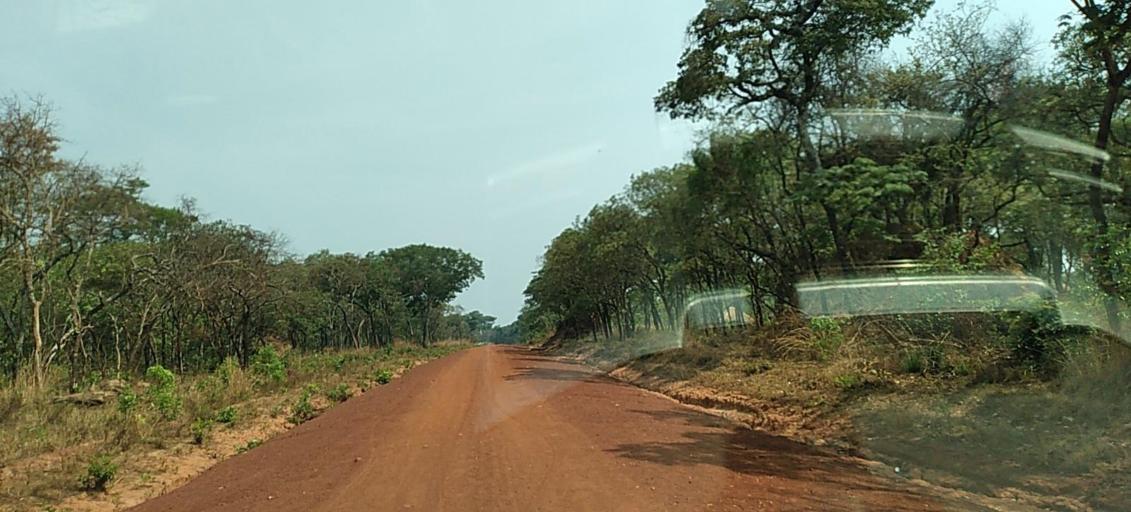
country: ZM
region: North-Western
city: Kansanshi
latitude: -12.0121
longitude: 26.8462
